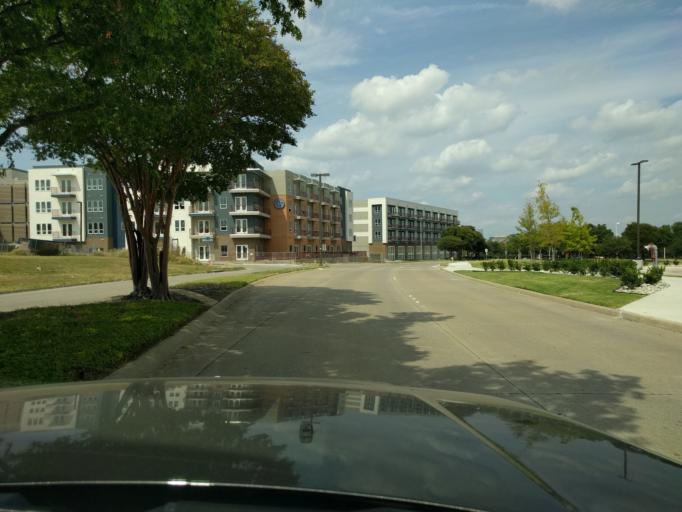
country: US
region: Texas
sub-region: Collin County
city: Plano
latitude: 32.9812
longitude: -96.7068
